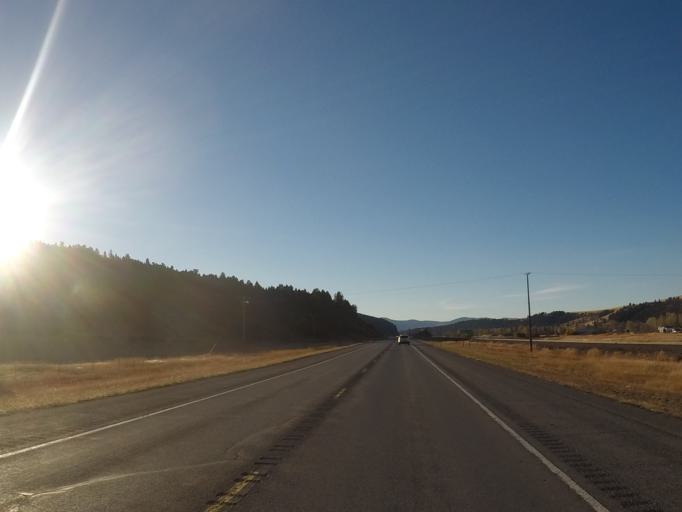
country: US
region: Montana
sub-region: Lewis and Clark County
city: Helena West Side
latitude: 46.5628
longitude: -112.4370
